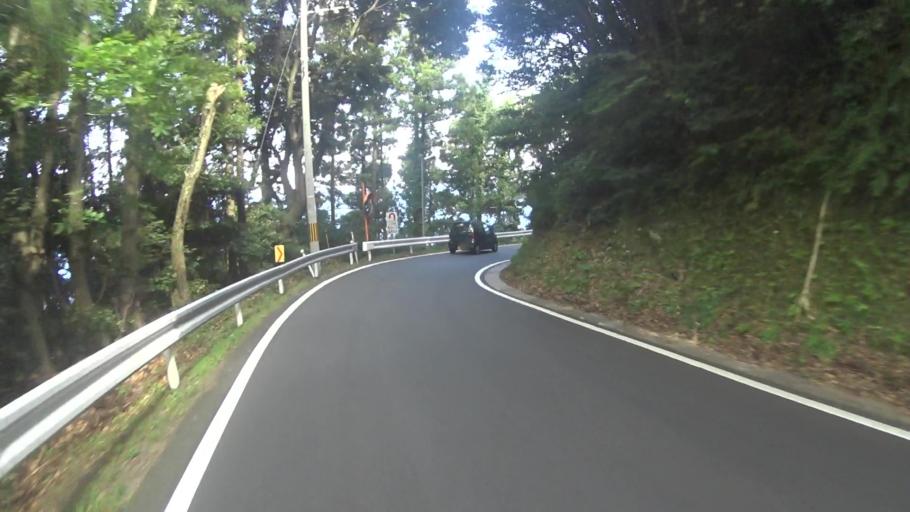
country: JP
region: Kyoto
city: Miyazu
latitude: 35.7481
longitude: 135.2505
